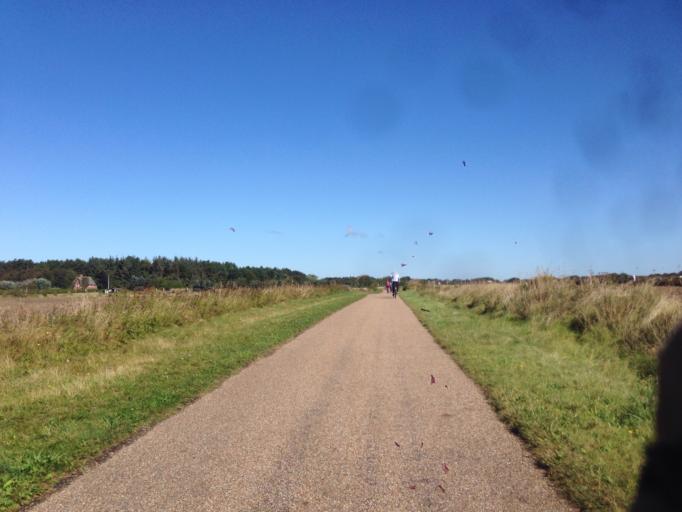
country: DE
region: Schleswig-Holstein
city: Tinnum
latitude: 54.9407
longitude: 8.3315
